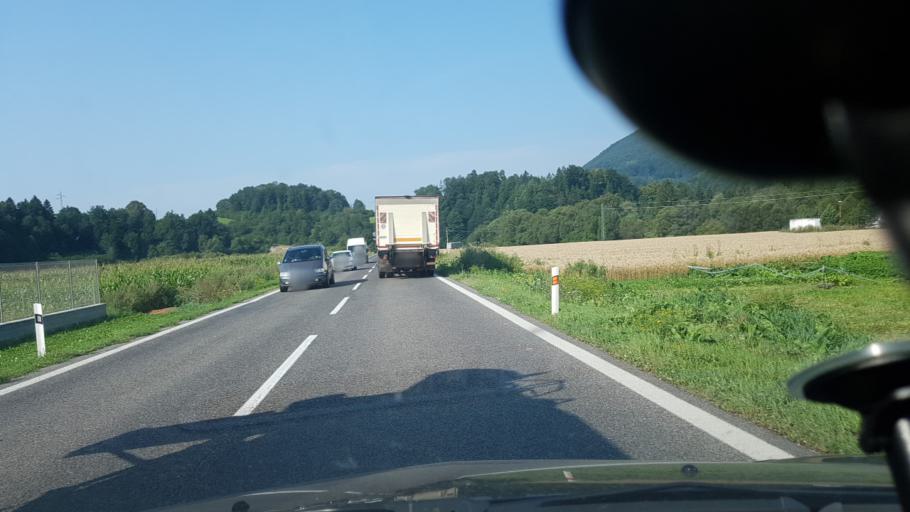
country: SK
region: Zilinsky
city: Tvrdosin
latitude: 49.2808
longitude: 19.4730
